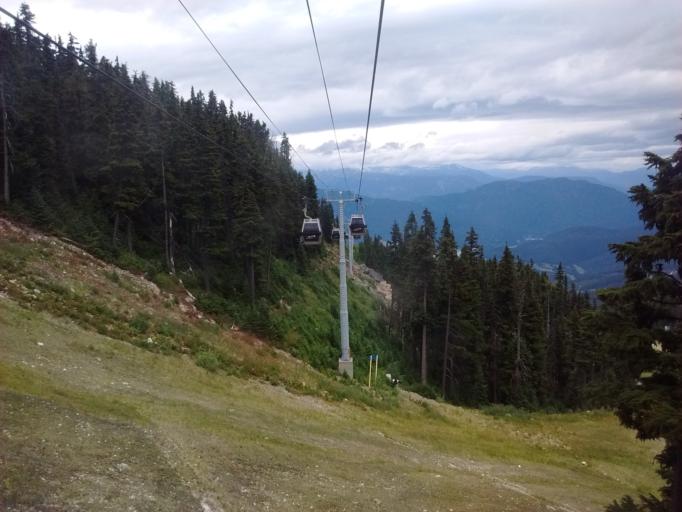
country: CA
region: British Columbia
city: Whistler
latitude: 50.0794
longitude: -122.9485
